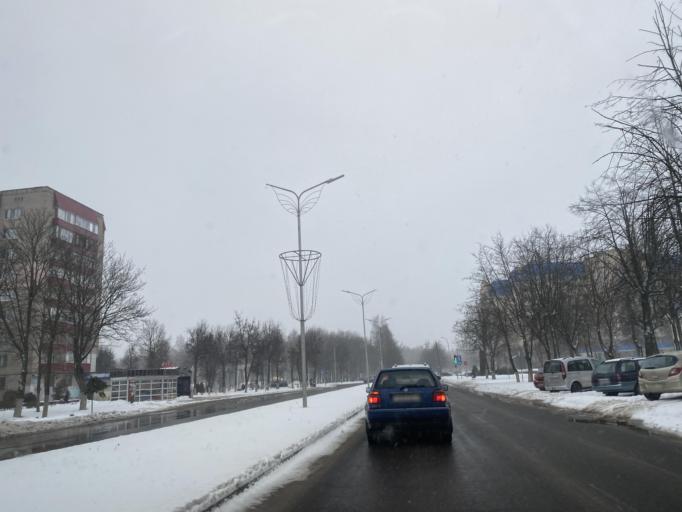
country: BY
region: Minsk
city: Horad Zhodzina
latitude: 54.0925
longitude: 28.3097
